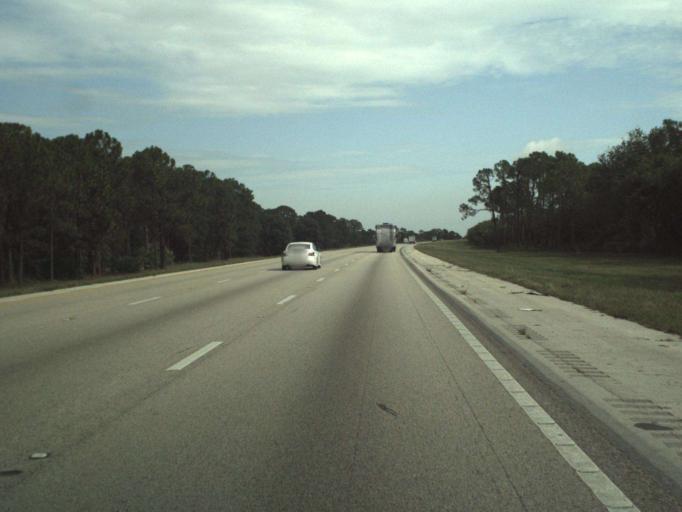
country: US
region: Florida
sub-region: Saint Lucie County
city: Port Saint Lucie
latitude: 27.1747
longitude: -80.3947
